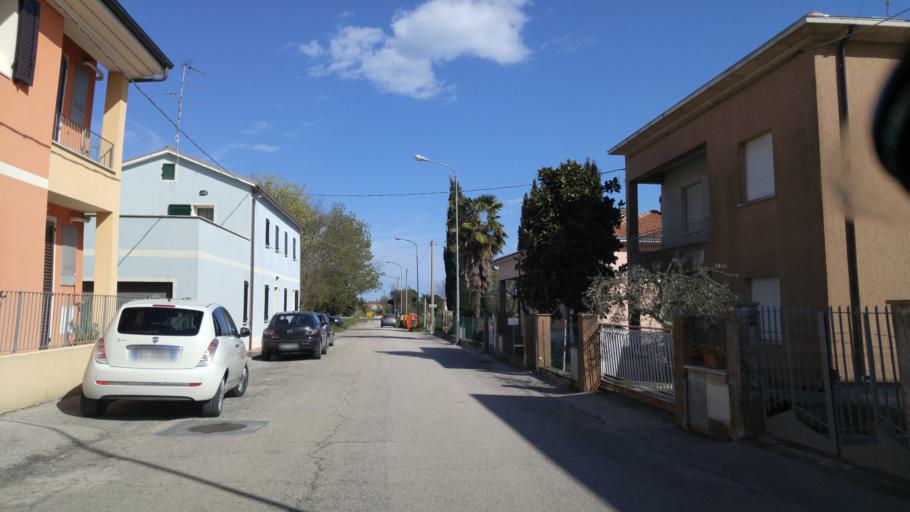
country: IT
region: The Marches
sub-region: Provincia di Pesaro e Urbino
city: Centinarola
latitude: 43.8407
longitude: 12.9888
